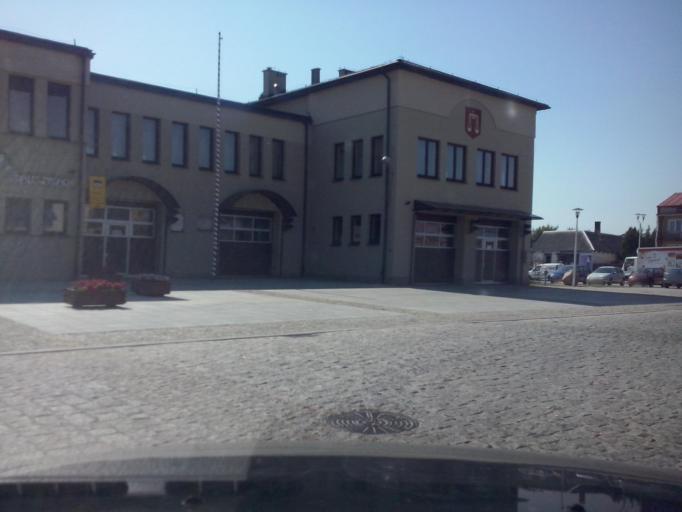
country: PL
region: Swietokrzyskie
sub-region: Powiat kielecki
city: Daleszyce
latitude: 50.8022
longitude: 20.8059
